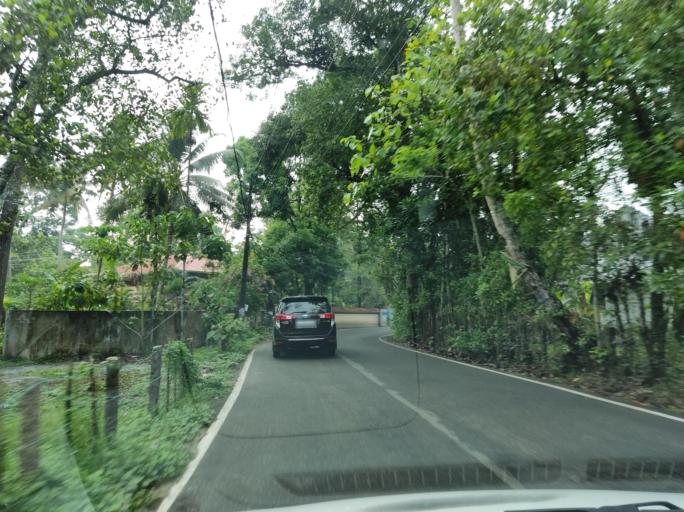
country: IN
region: Kerala
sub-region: Alappuzha
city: Kayankulam
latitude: 9.2015
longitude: 76.4641
